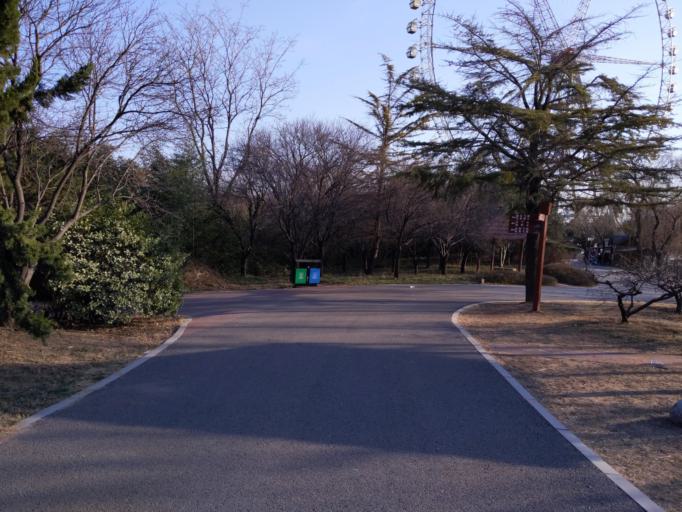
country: CN
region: Henan Sheng
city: Puyang
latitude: 35.7767
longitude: 114.9595
